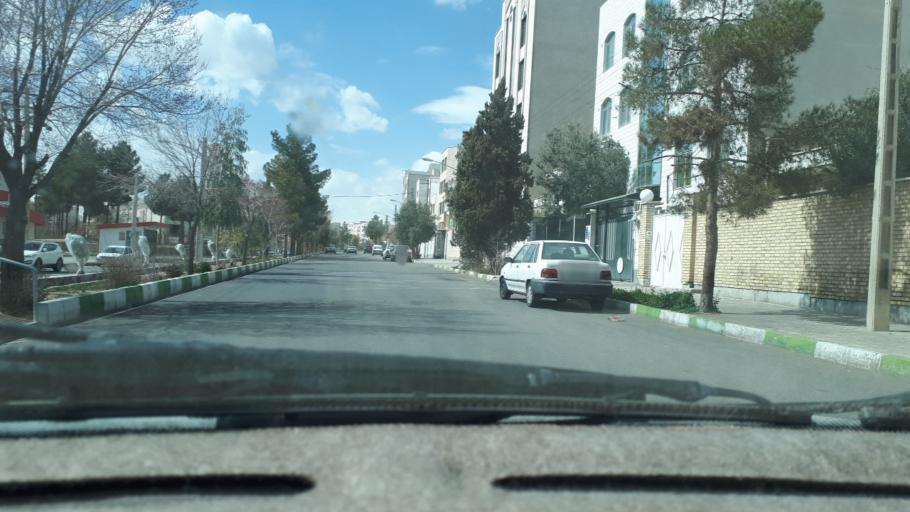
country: IR
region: Semnan
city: Semnan
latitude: 35.5806
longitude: 53.3816
